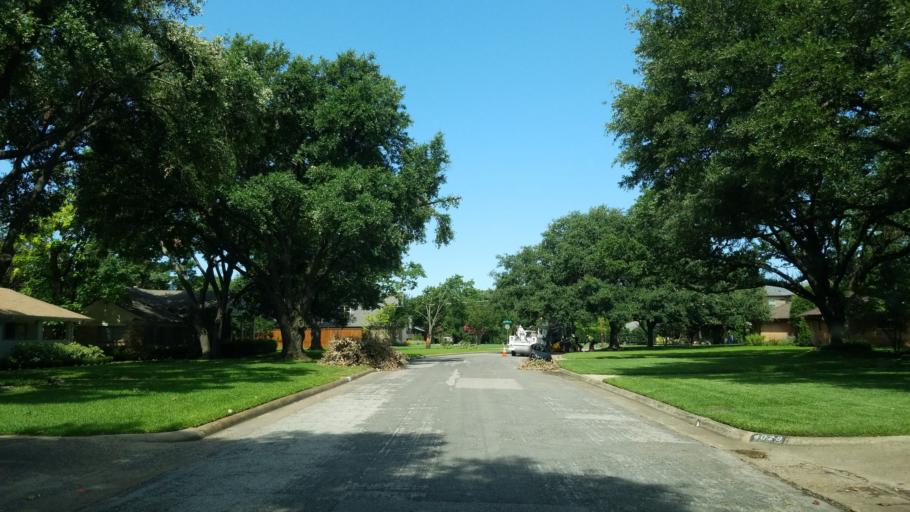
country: US
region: Texas
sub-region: Dallas County
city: Addison
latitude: 32.9079
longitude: -96.8425
